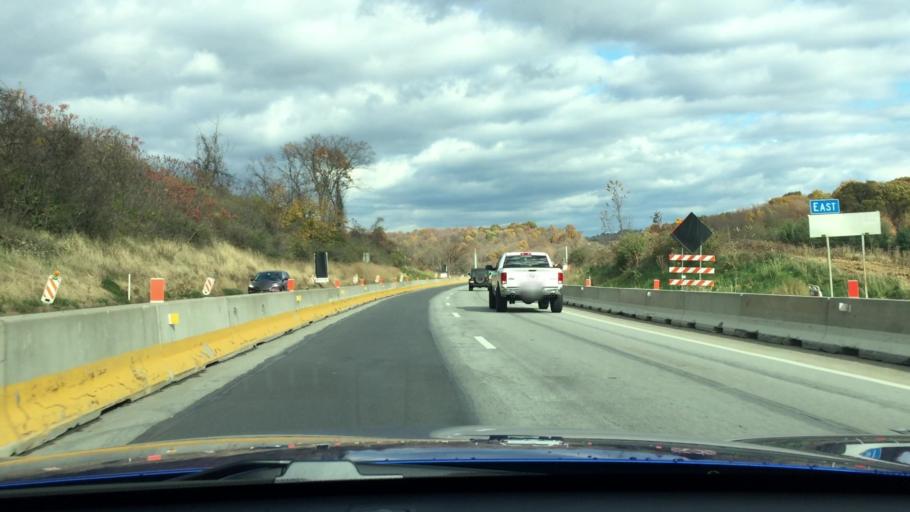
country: US
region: Pennsylvania
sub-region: Westmoreland County
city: West Newton
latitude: 40.1868
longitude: -79.7063
